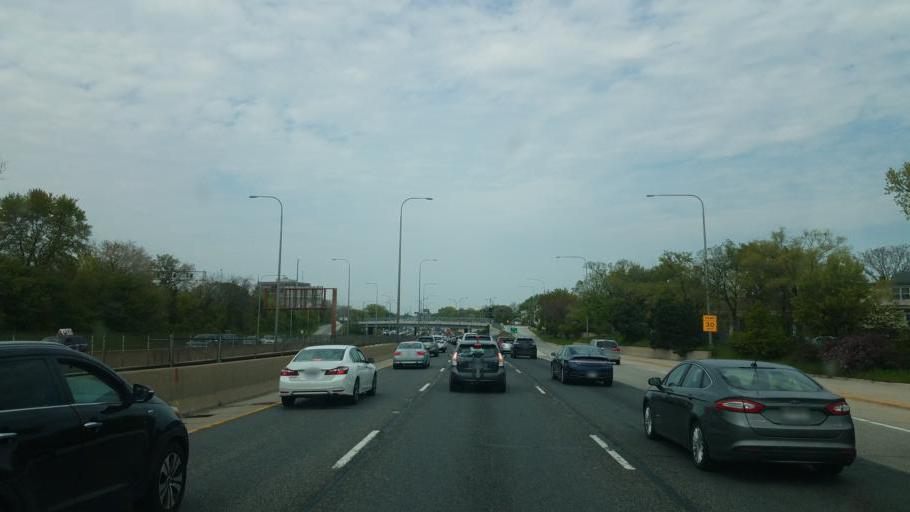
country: US
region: Illinois
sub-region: Cook County
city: Lincolnwood
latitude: 41.9660
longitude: -87.7524
